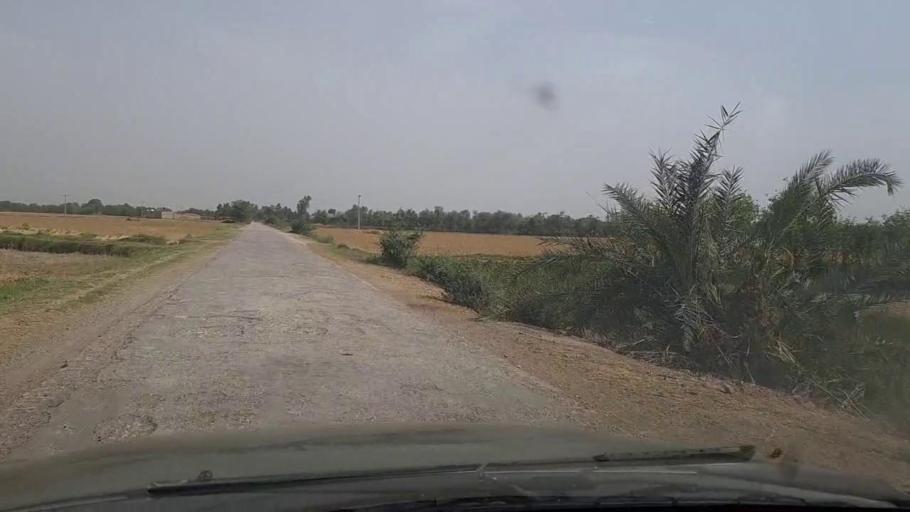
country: PK
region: Sindh
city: Lakhi
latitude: 27.8455
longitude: 68.7574
